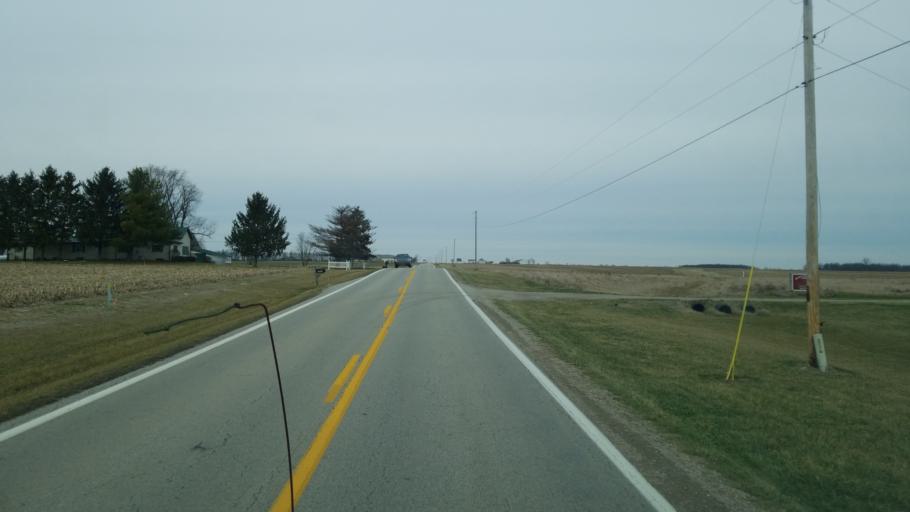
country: US
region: Ohio
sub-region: Ross County
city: Frankfort
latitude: 39.4567
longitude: -83.2099
